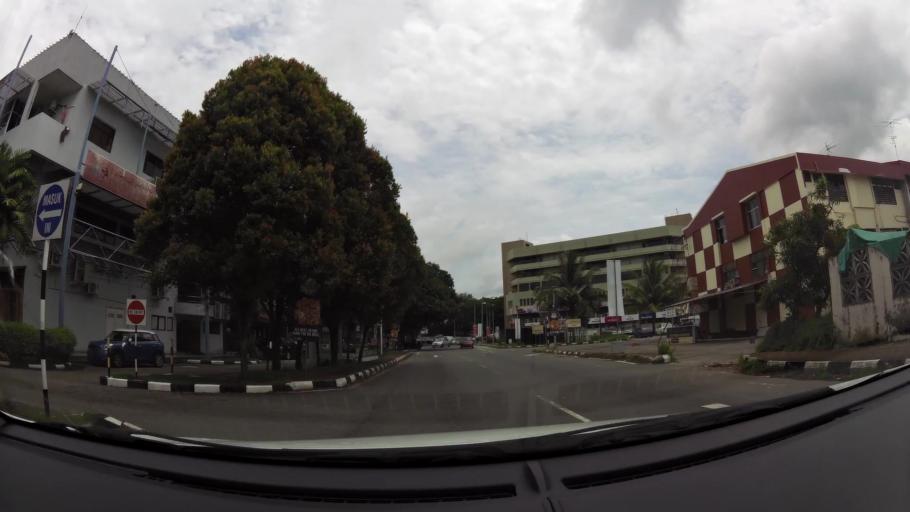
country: BN
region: Brunei and Muara
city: Bandar Seri Begawan
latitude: 4.9081
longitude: 114.9154
